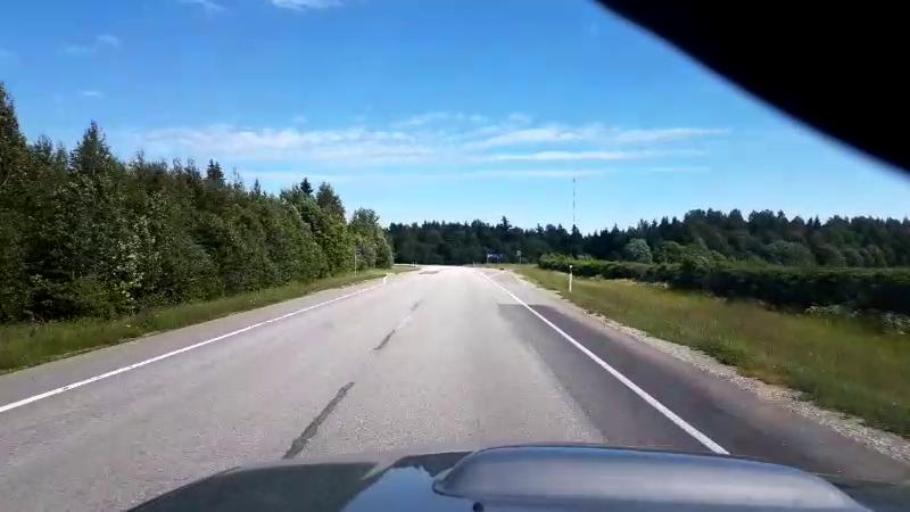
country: EE
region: Jaervamaa
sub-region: Koeru vald
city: Koeru
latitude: 58.9857
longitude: 26.0080
